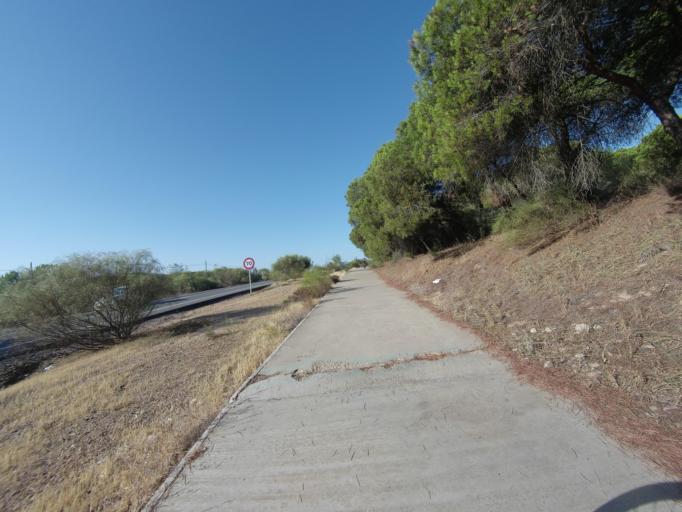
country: ES
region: Andalusia
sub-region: Provincia de Huelva
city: Aljaraque
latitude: 37.2074
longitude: -7.0282
